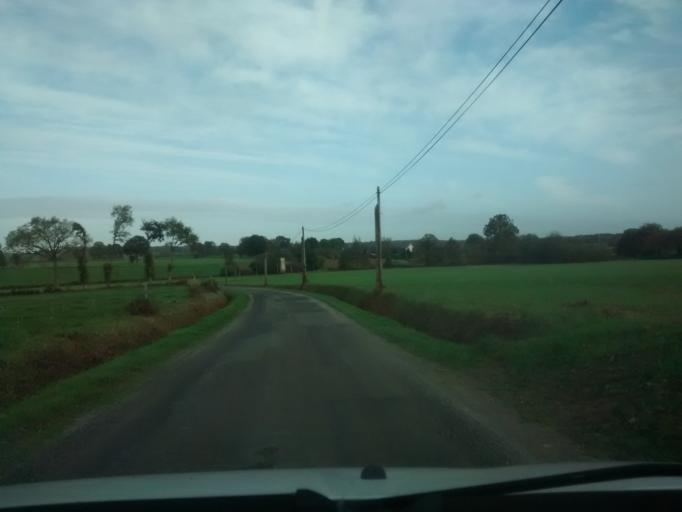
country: FR
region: Brittany
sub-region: Departement d'Ille-et-Vilaine
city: Servon-sur-Vilaine
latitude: 48.1366
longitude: -1.4738
